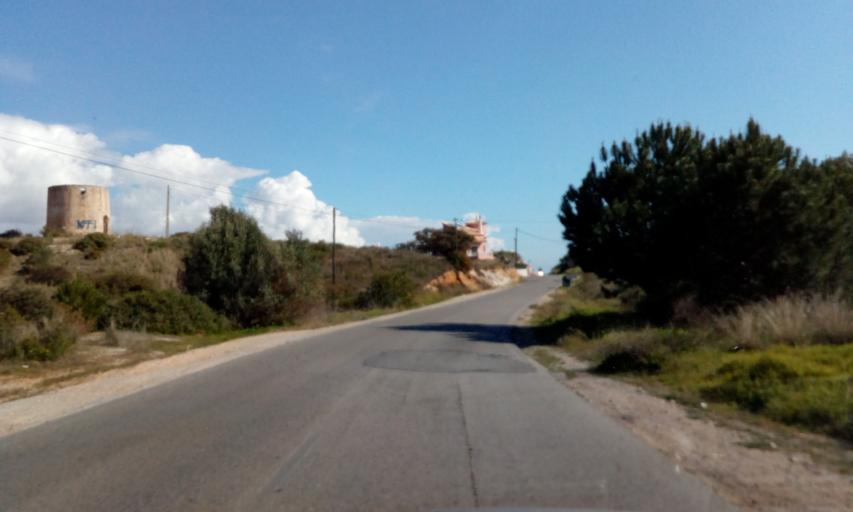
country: PT
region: Faro
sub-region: Albufeira
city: Ferreiras
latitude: 37.1182
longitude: -8.2161
